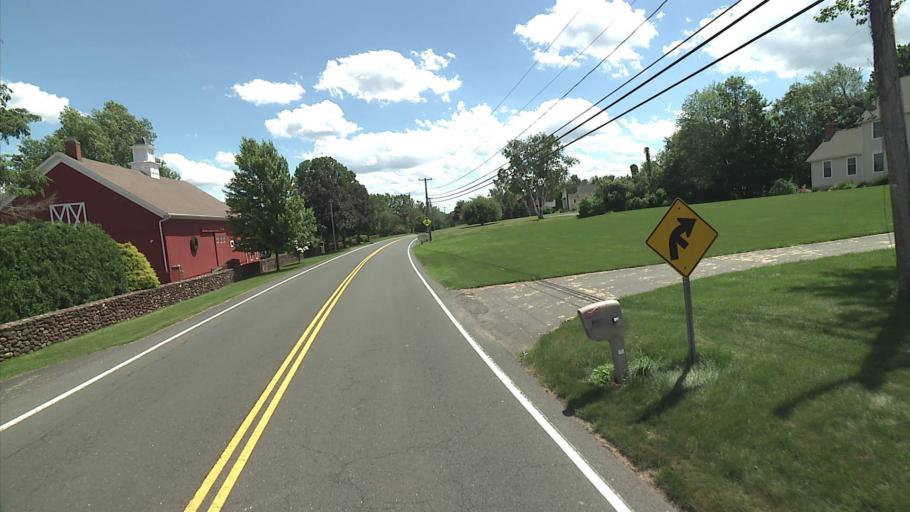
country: US
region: Massachusetts
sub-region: Hampden County
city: East Longmeadow
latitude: 42.0225
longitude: -72.4850
